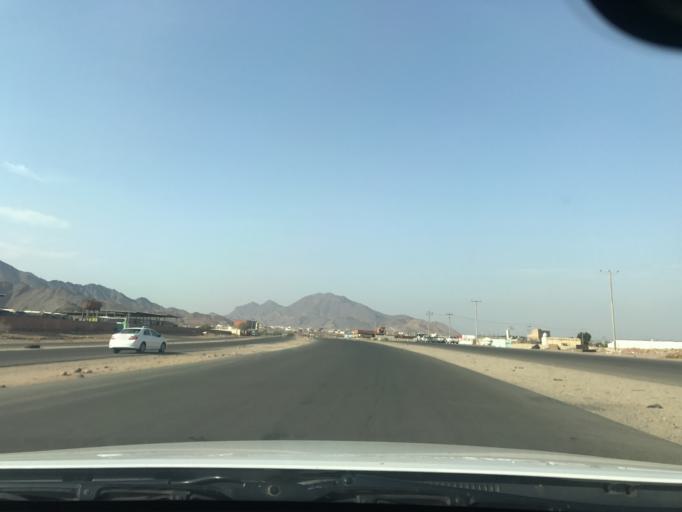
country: SA
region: Makkah
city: Al Jumum
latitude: 21.4442
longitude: 39.5181
